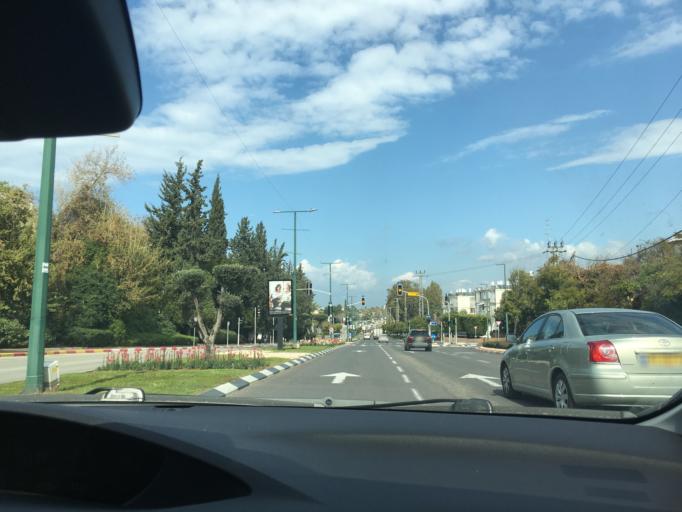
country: IL
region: Central District
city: Ra'anana
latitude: 32.1725
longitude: 34.8521
